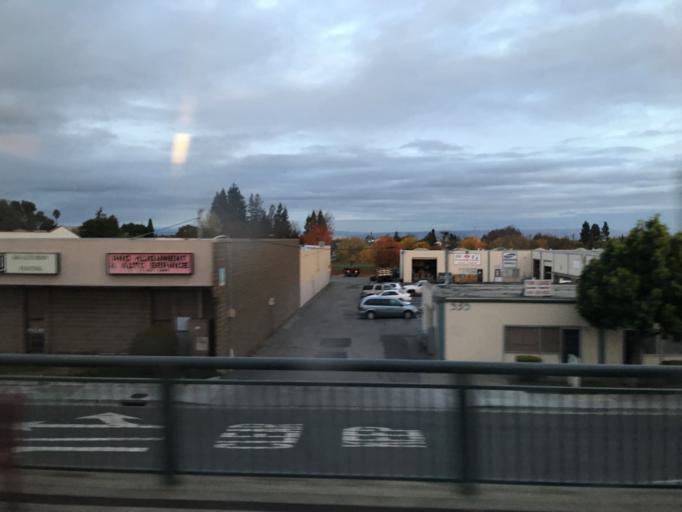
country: US
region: California
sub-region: San Mateo County
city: San Carlos
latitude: 37.5086
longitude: -122.2607
